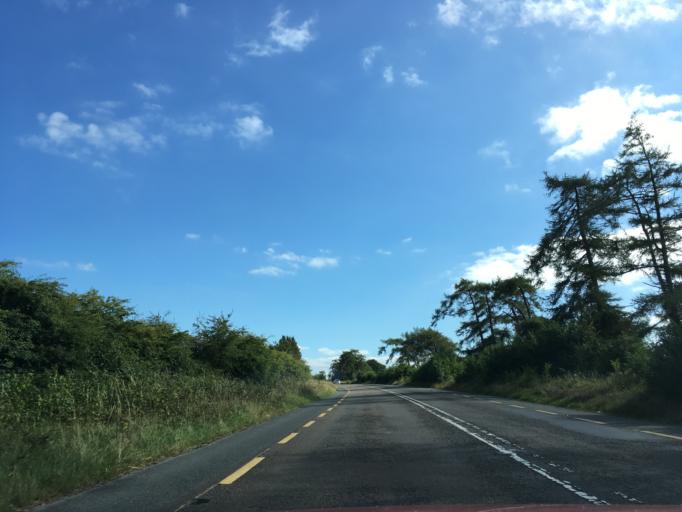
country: IE
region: Munster
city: Cashel
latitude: 52.4809
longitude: -7.8920
